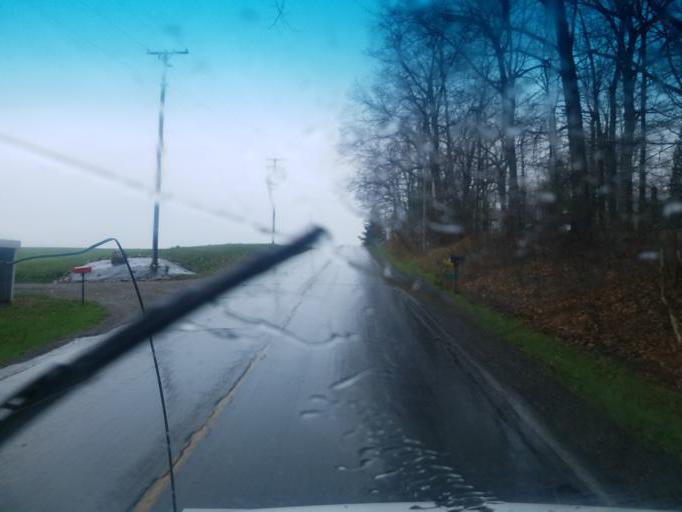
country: US
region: Ohio
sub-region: Wayne County
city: Apple Creek
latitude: 40.7018
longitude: -81.8862
